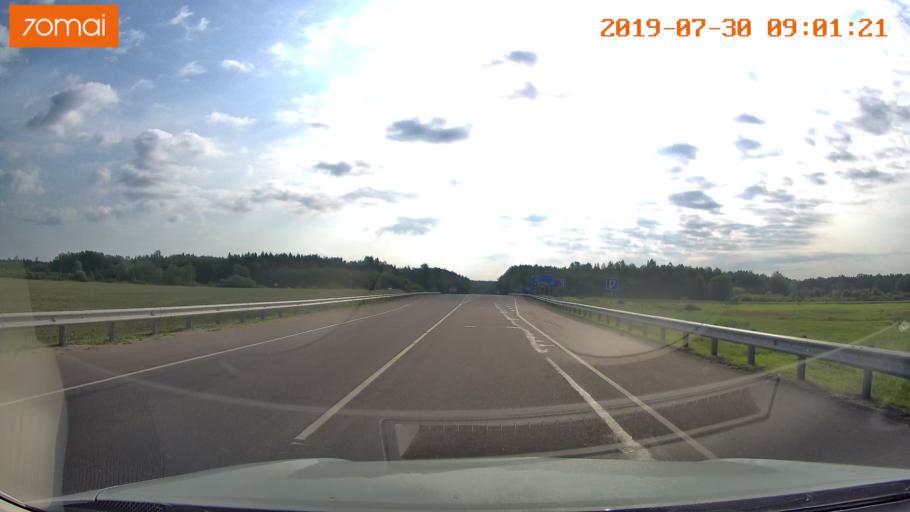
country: RU
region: Kaliningrad
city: Gusev
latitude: 54.6164
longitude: 22.2045
